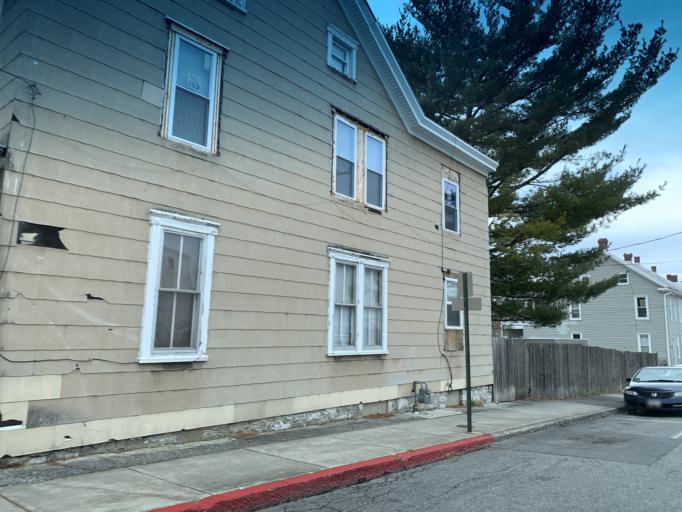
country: US
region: Maryland
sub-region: Washington County
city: Hagerstown
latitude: 39.6358
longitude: -77.7198
